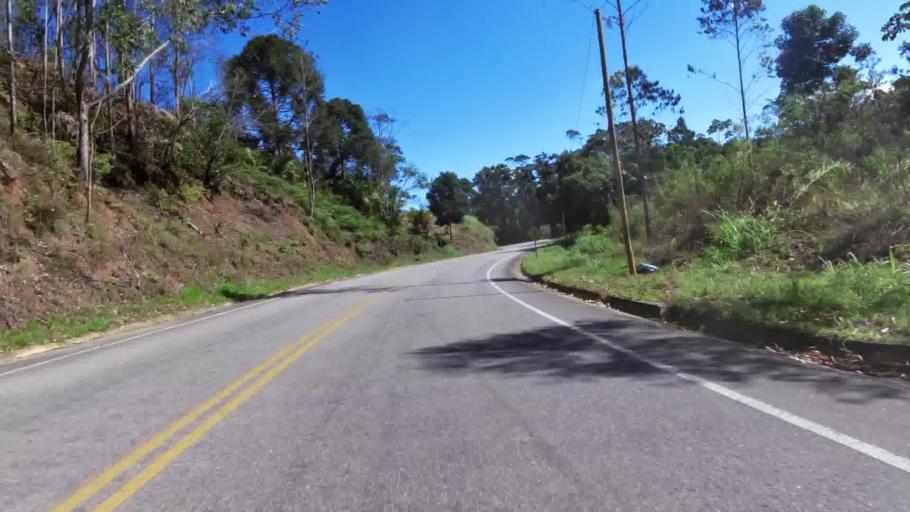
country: BR
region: Espirito Santo
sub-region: Vargem Alta
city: Vargem Alta
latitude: -20.6838
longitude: -40.9495
